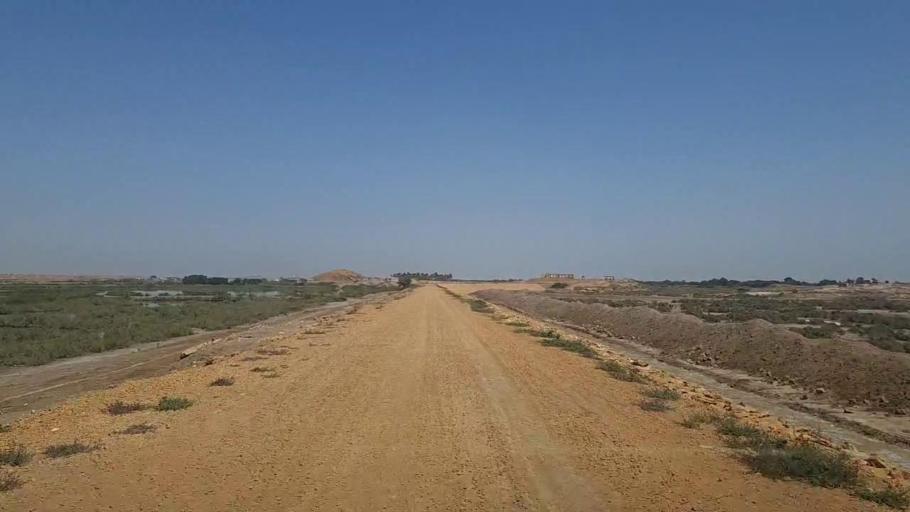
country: PK
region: Sindh
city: Thatta
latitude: 24.8042
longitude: 68.0017
